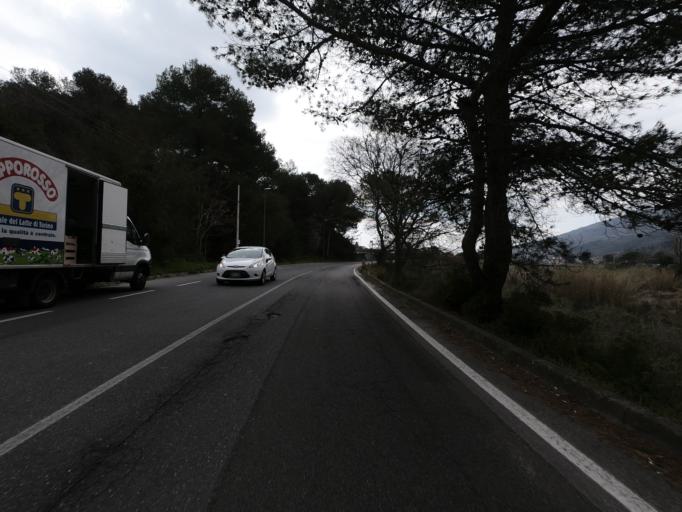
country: IT
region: Liguria
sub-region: Provincia di Savona
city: Laigueglia
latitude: 43.9817
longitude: 8.1343
